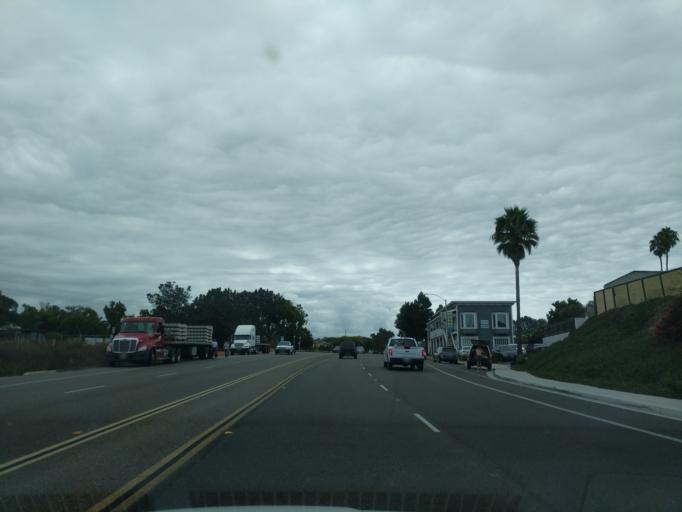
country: US
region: California
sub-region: San Diego County
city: Solana Beach
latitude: 33.0005
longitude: -117.2756
